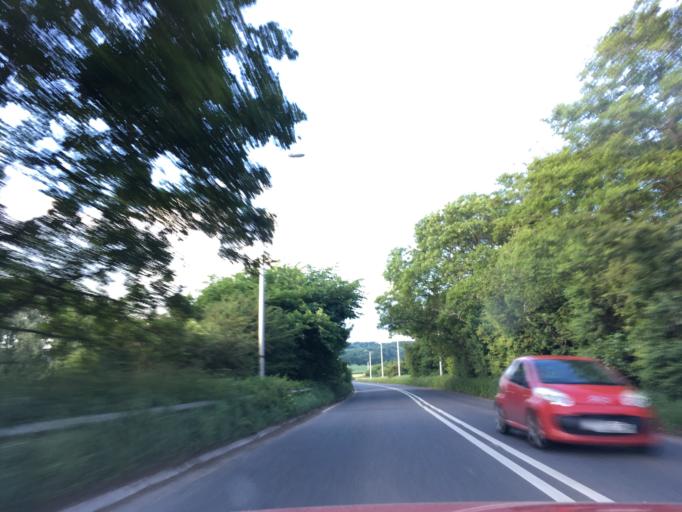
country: GB
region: England
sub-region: North Somerset
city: Wrington
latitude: 51.3506
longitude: -2.7479
